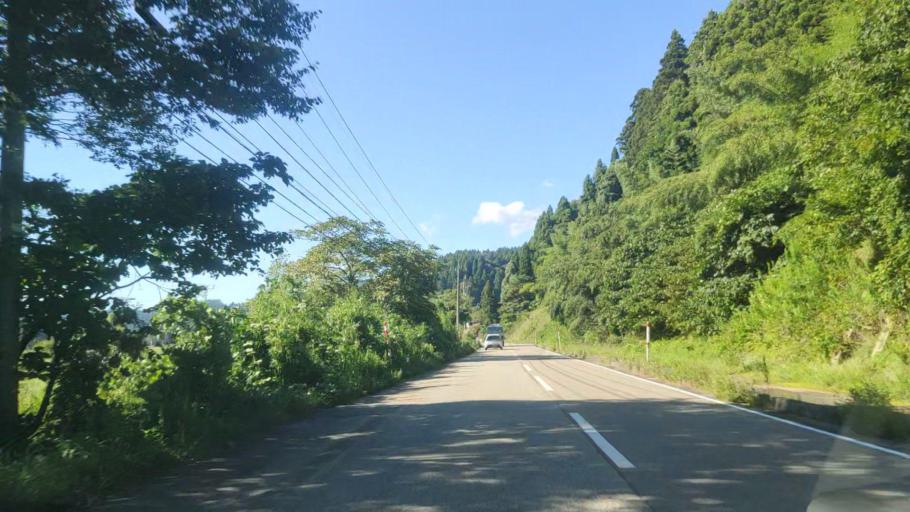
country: JP
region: Ishikawa
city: Nanao
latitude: 37.2750
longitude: 137.0541
